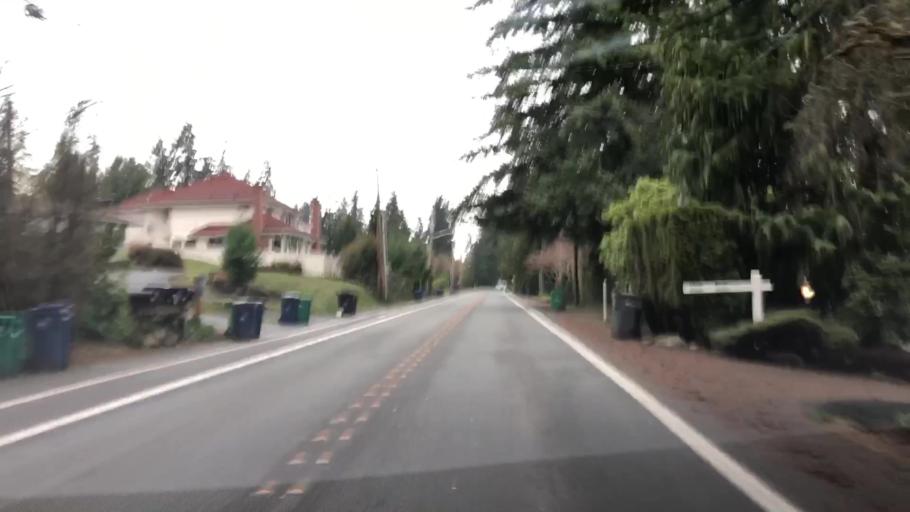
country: US
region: Washington
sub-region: King County
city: Sammamish
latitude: 47.6379
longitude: -122.0957
